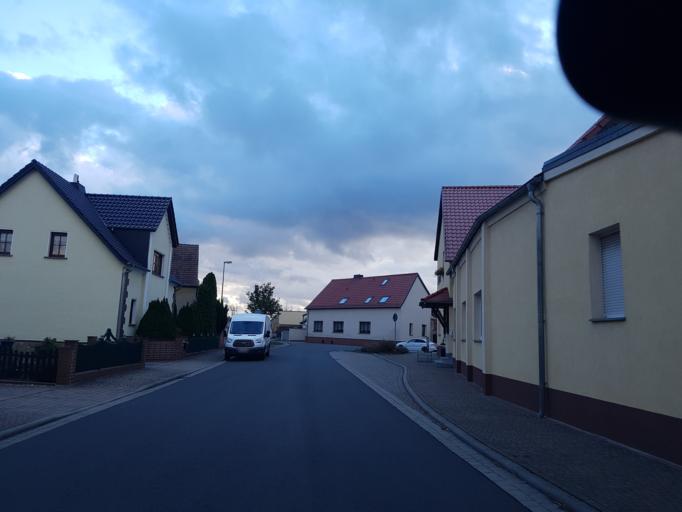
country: DE
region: Saxony-Anhalt
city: Elster
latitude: 51.8210
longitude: 12.8536
